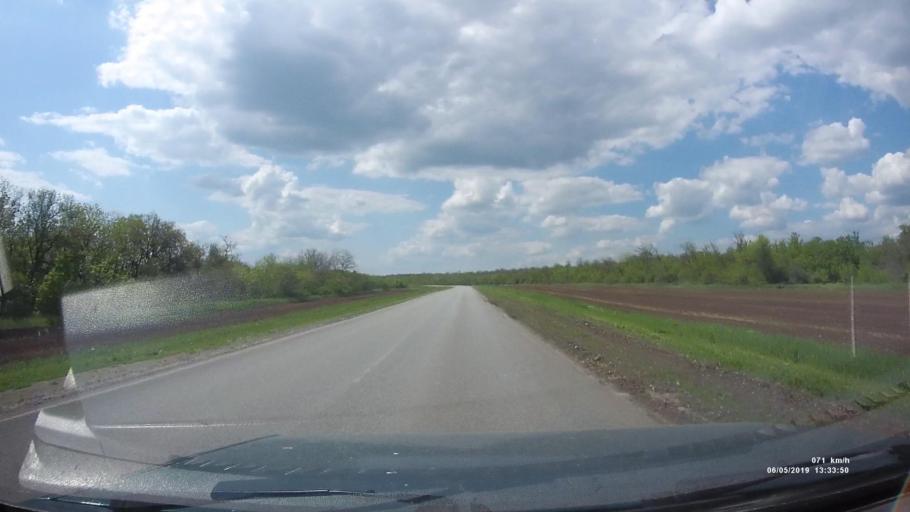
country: RU
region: Rostov
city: Ust'-Donetskiy
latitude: 47.6919
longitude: 40.7731
